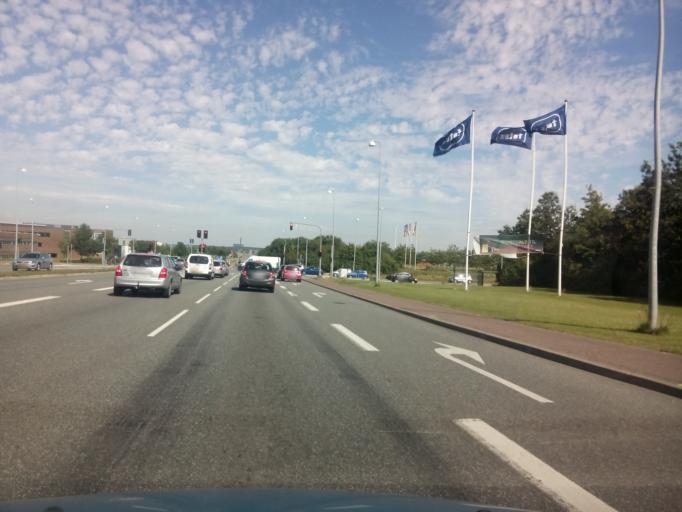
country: DK
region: Central Jutland
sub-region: Arhus Kommune
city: Arhus
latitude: 56.1924
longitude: 10.1878
